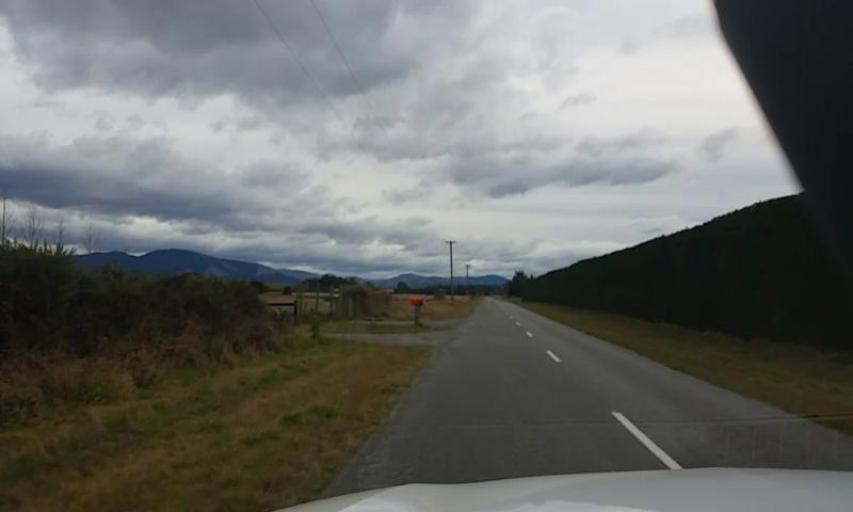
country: NZ
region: Canterbury
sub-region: Waimakariri District
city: Kaiapoi
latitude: -43.2943
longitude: 172.4375
